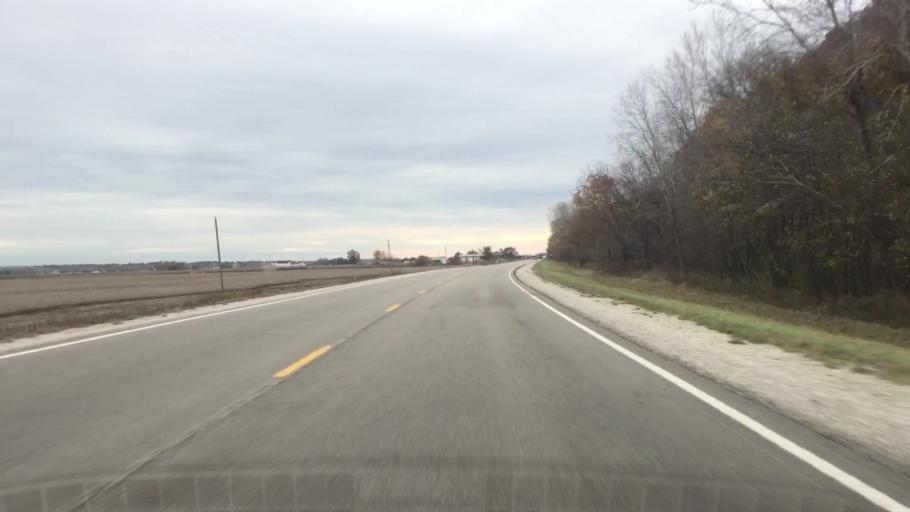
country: US
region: Missouri
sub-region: Cole County
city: Jefferson City
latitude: 38.5874
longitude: -92.1243
